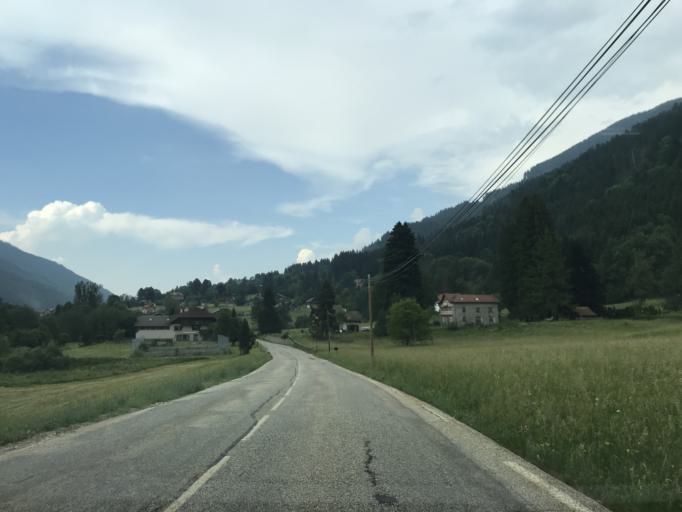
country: FR
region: Rhone-Alpes
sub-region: Departement de l'Isere
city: Theys
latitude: 45.3003
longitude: 6.0806
